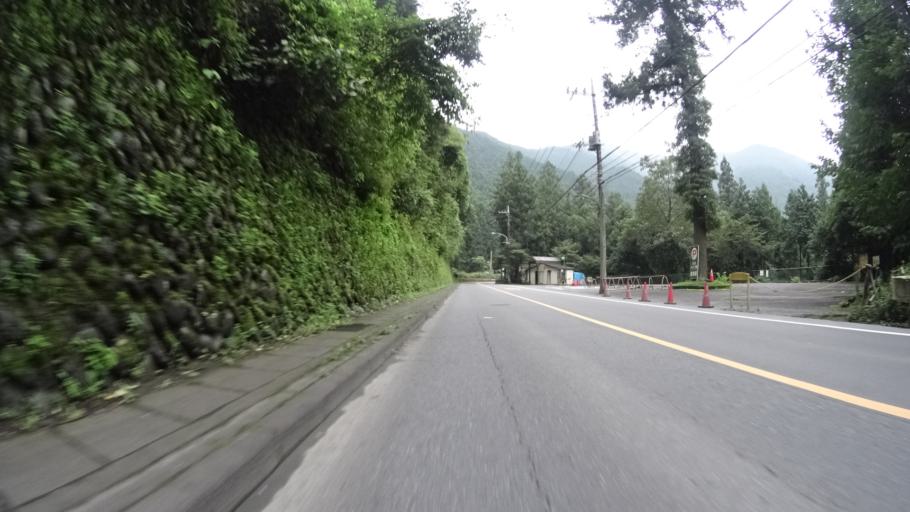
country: JP
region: Tokyo
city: Ome
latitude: 35.8087
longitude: 139.1631
